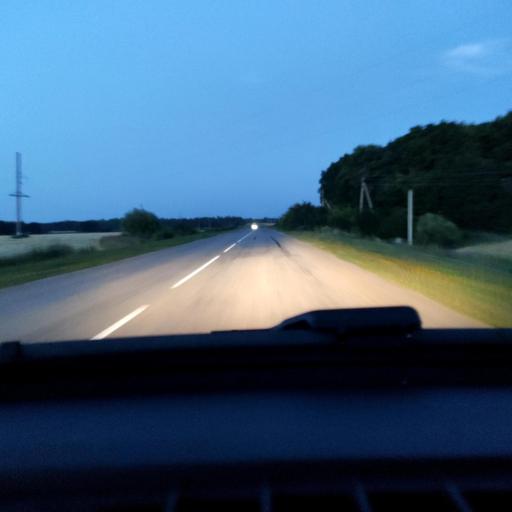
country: RU
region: Lipetsk
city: Zadonsk
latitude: 52.2971
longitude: 38.8239
